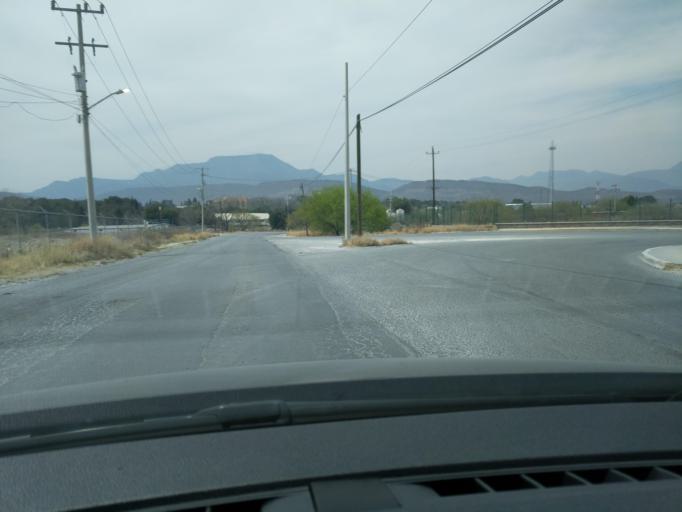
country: MX
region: Coahuila
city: Saltillo
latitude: 25.3530
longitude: -101.0240
